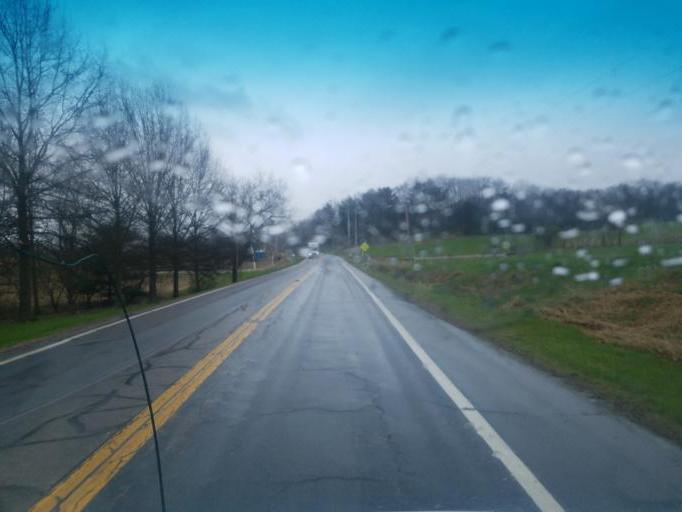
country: US
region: Ohio
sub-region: Wayne County
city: Wooster
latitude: 40.7384
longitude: -81.9356
